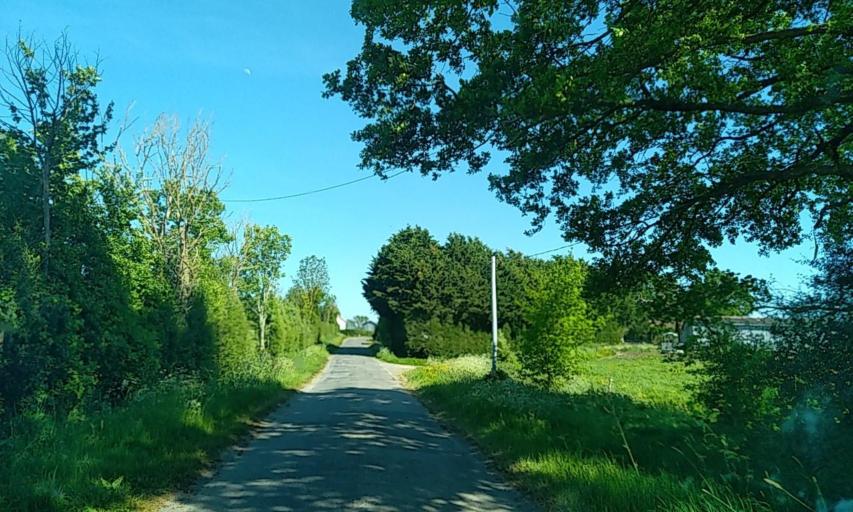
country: FR
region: Poitou-Charentes
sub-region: Departement des Deux-Sevres
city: Boisme
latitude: 46.7712
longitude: -0.4101
